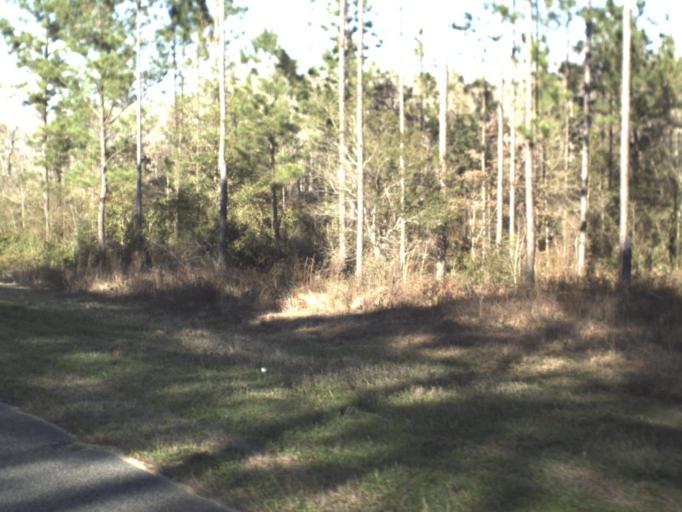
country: US
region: Florida
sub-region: Jackson County
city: Marianna
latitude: 30.6074
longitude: -85.1811
